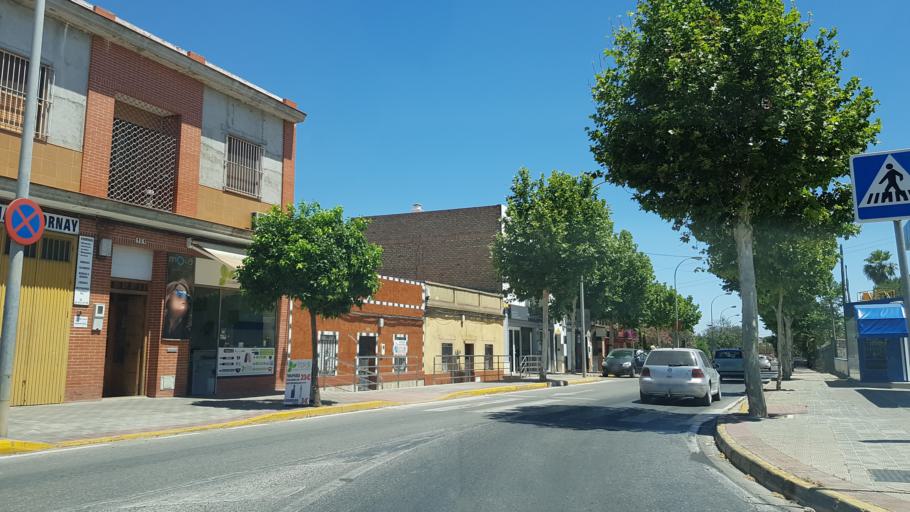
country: ES
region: Andalusia
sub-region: Provincia de Sevilla
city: Dos Hermanas
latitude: 37.2877
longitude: -5.9059
